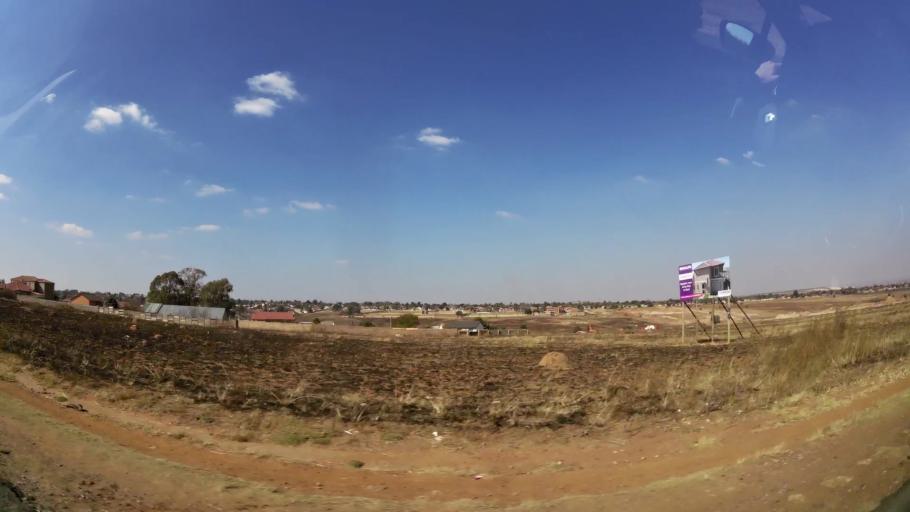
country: ZA
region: Gauteng
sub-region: City of Johannesburg Metropolitan Municipality
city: Roodepoort
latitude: -26.1451
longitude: 27.8145
